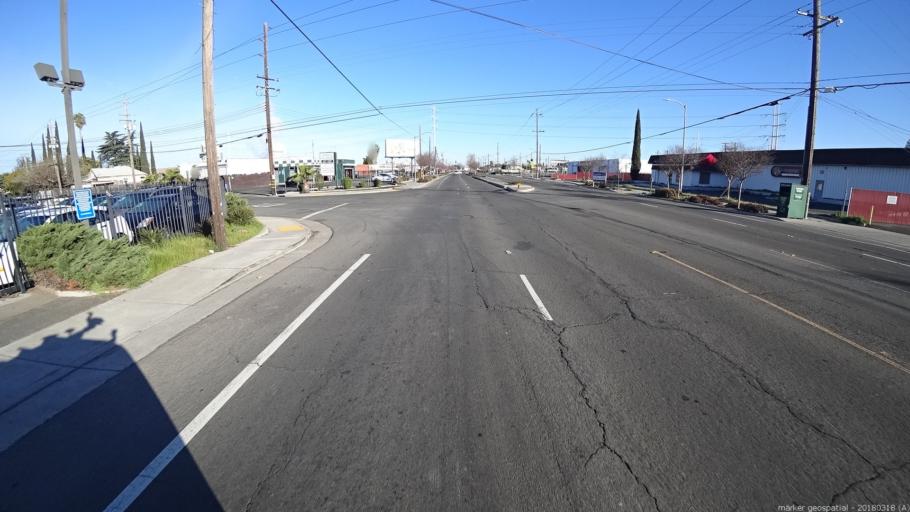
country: US
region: California
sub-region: Sacramento County
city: Parkway
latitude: 38.5048
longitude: -121.4641
